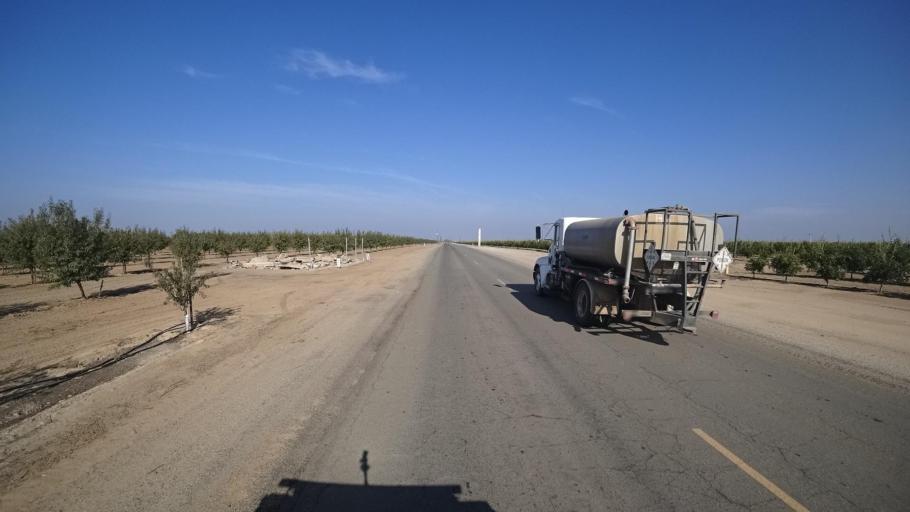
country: US
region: California
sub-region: Kern County
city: McFarland
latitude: 35.6552
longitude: -119.1691
